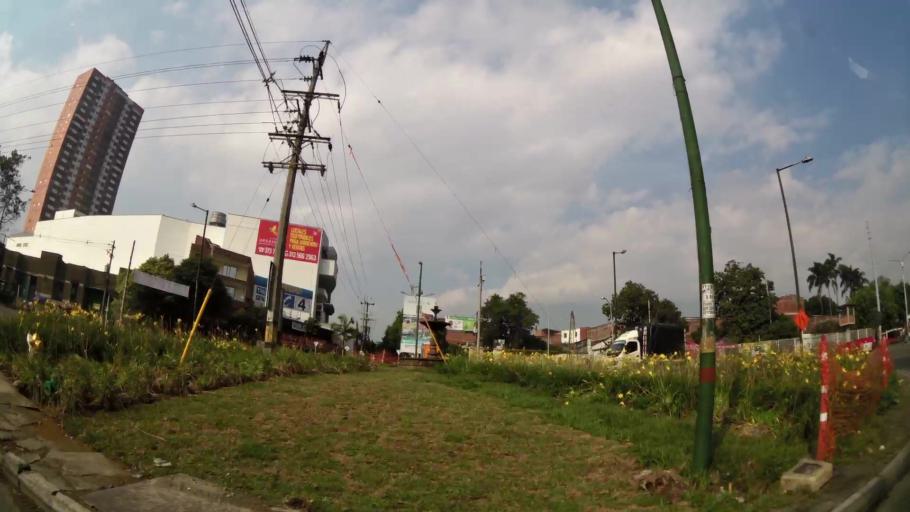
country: CO
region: Antioquia
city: Sabaneta
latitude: 6.1683
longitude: -75.6189
